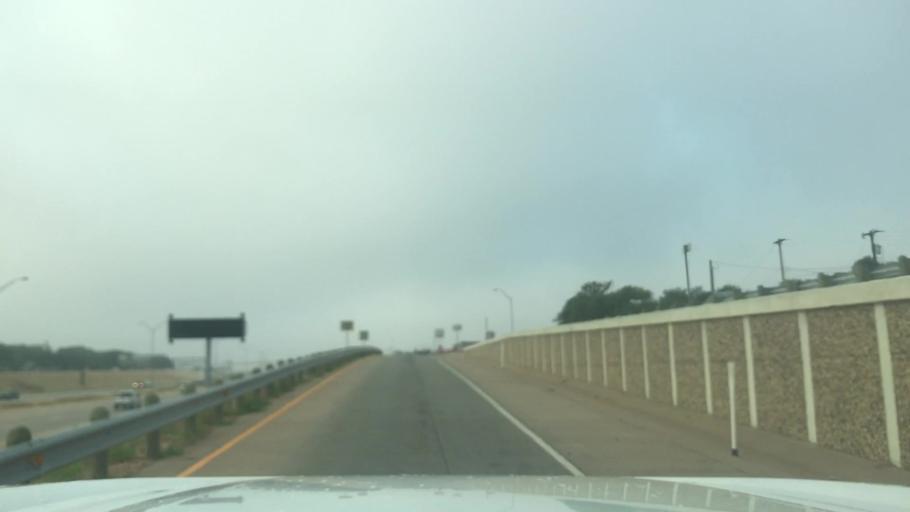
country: US
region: Texas
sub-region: Lubbock County
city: Lubbock
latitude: 33.5463
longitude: -101.8455
